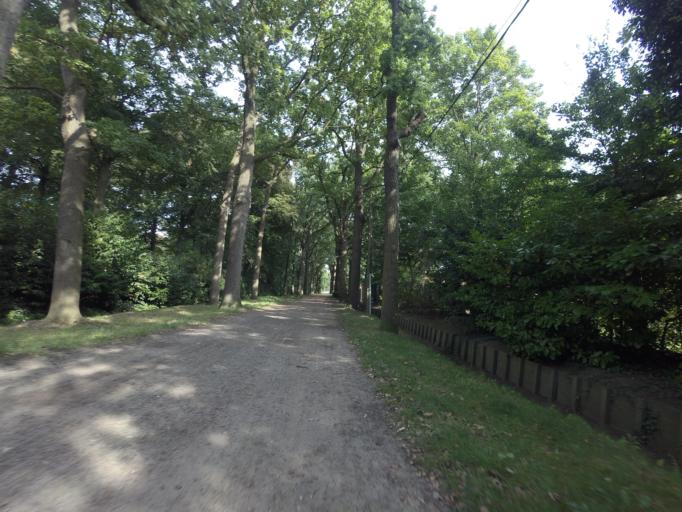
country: BE
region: Flanders
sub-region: Provincie Antwerpen
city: Aartselaar
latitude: 51.1396
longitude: 4.4053
